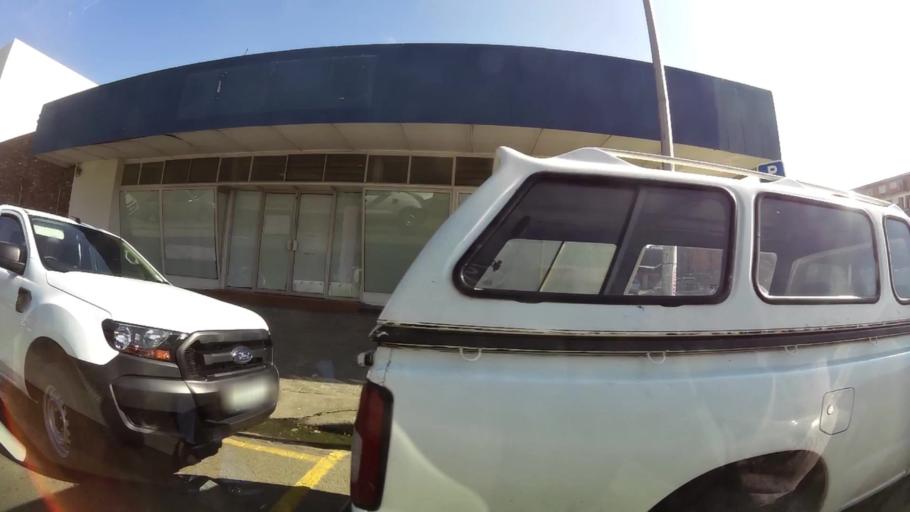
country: ZA
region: Orange Free State
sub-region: Mangaung Metropolitan Municipality
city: Bloemfontein
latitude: -29.1128
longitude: 26.2230
